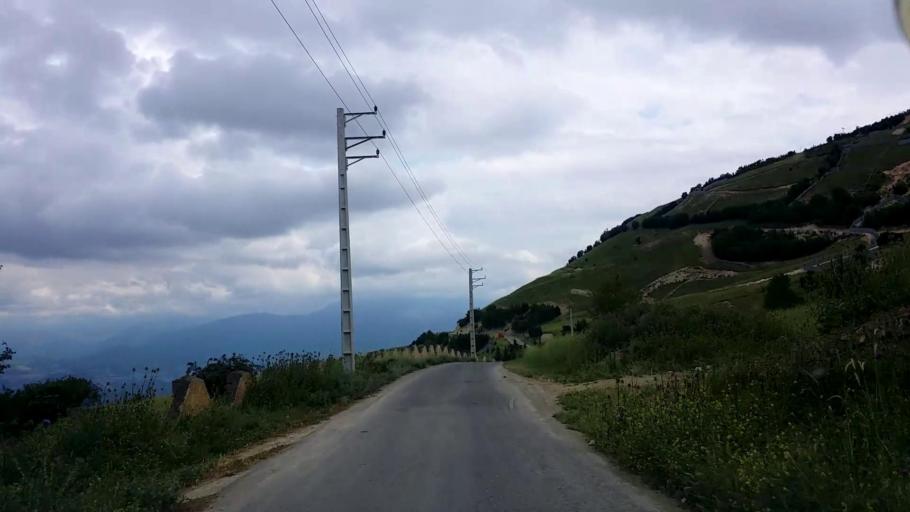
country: IR
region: Mazandaran
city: Chalus
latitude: 36.5466
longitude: 51.2709
